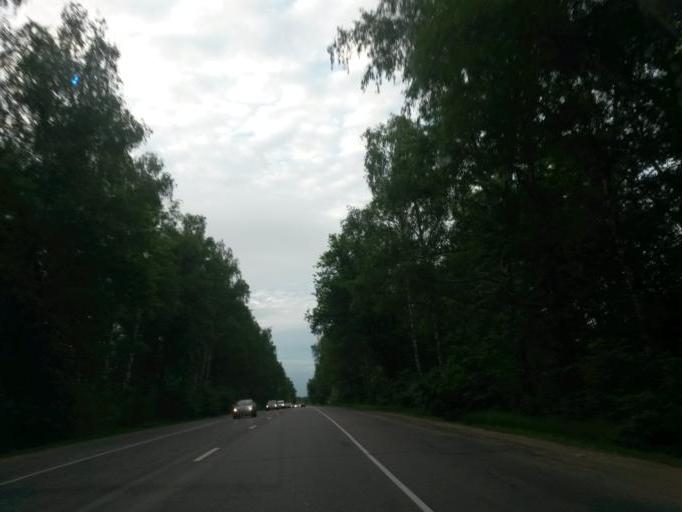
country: RU
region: Moskovskaya
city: Stolbovaya
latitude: 55.2334
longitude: 37.5039
